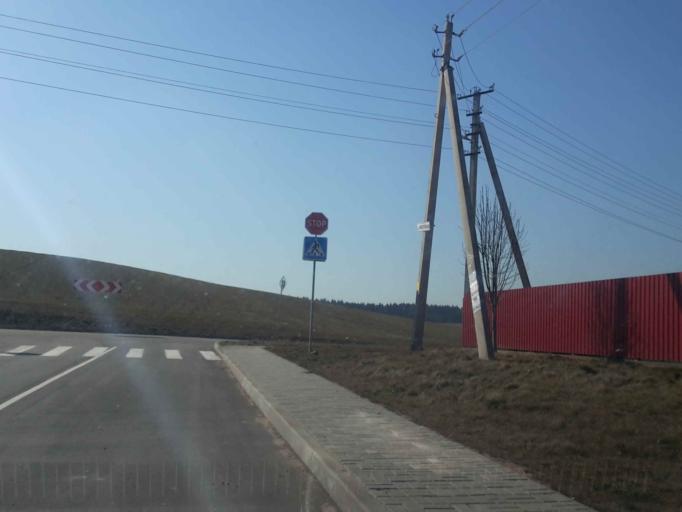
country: BY
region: Minsk
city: Zhdanovichy
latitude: 53.9170
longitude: 27.4067
